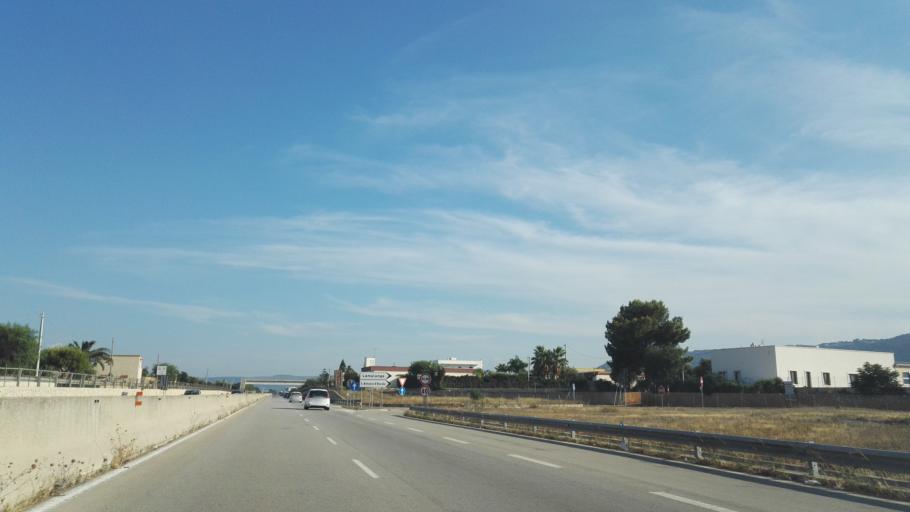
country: IT
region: Apulia
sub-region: Provincia di Brindisi
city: Fasano
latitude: 40.8713
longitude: 17.3424
